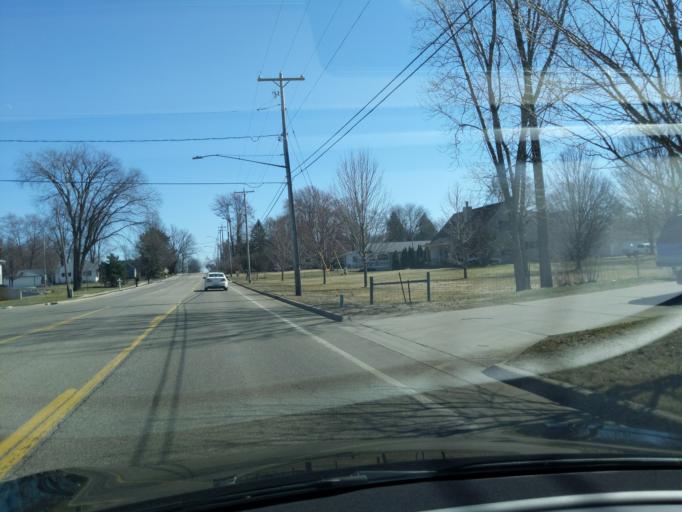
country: US
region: Michigan
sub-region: Ingham County
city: Holt
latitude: 42.6547
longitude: -84.5210
